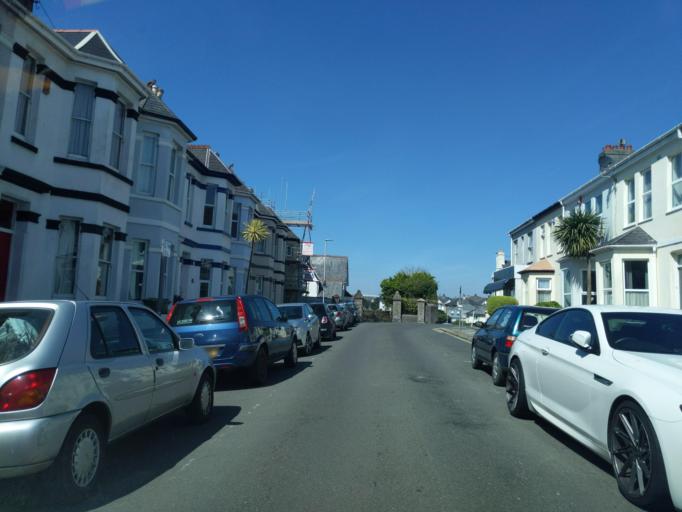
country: GB
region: England
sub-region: Plymouth
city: Plymouth
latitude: 50.3836
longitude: -4.1404
